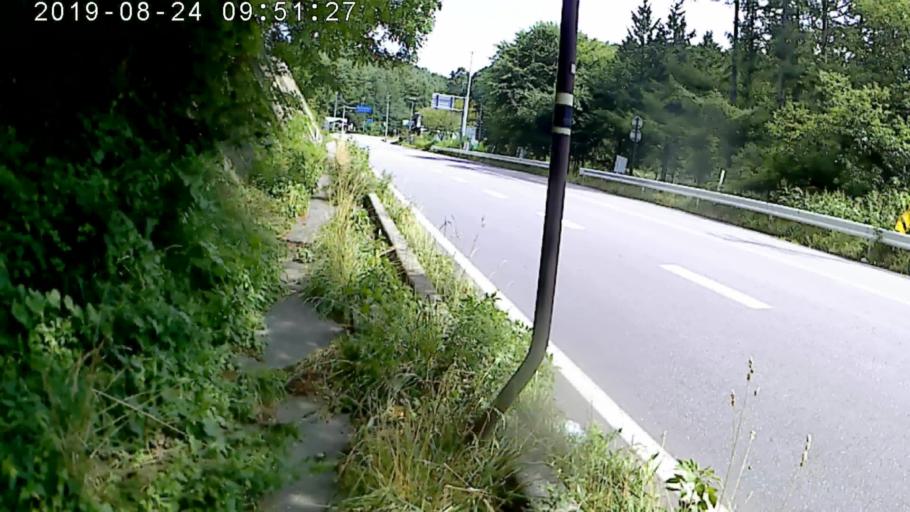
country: JP
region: Nagano
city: Kamimaruko
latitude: 36.2552
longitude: 138.2864
